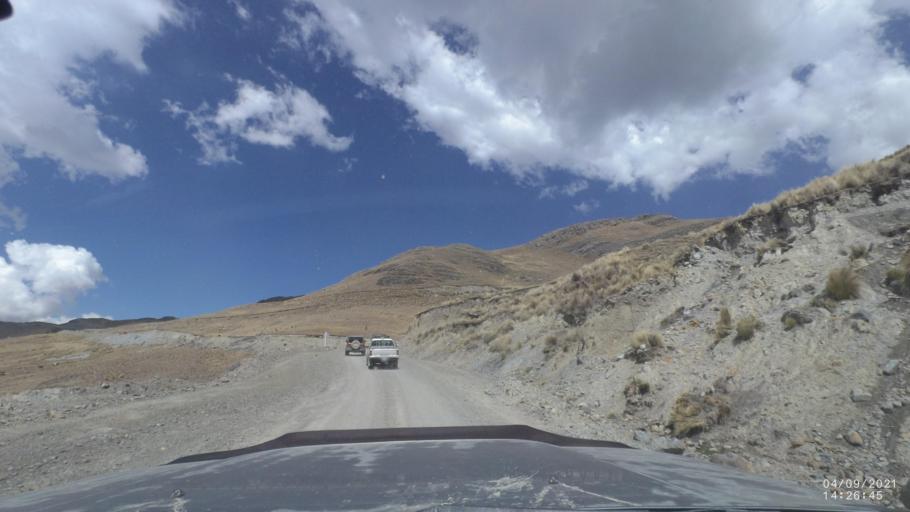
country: BO
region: Cochabamba
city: Sipe Sipe
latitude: -17.2443
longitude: -66.4080
